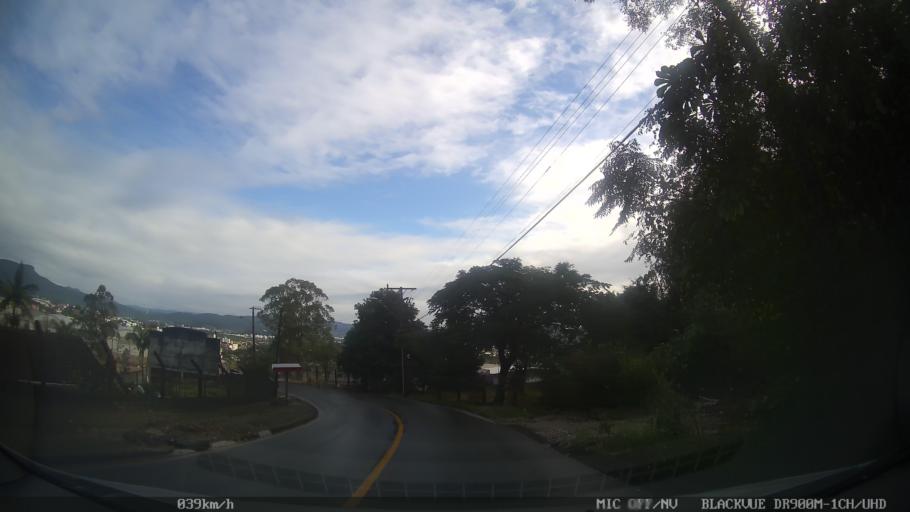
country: BR
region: Santa Catarina
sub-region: Sao Jose
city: Campinas
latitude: -27.6120
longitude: -48.6383
